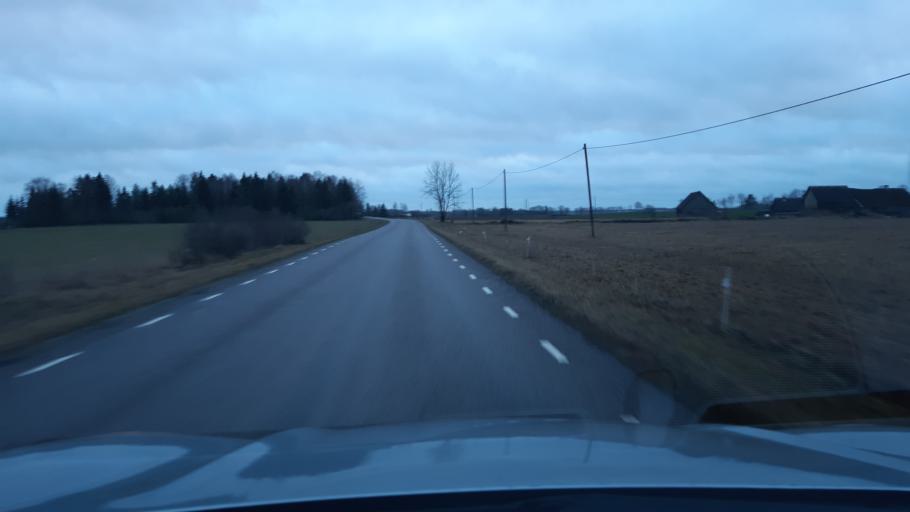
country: EE
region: Raplamaa
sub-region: Kohila vald
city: Kohila
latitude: 59.0728
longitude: 24.6813
